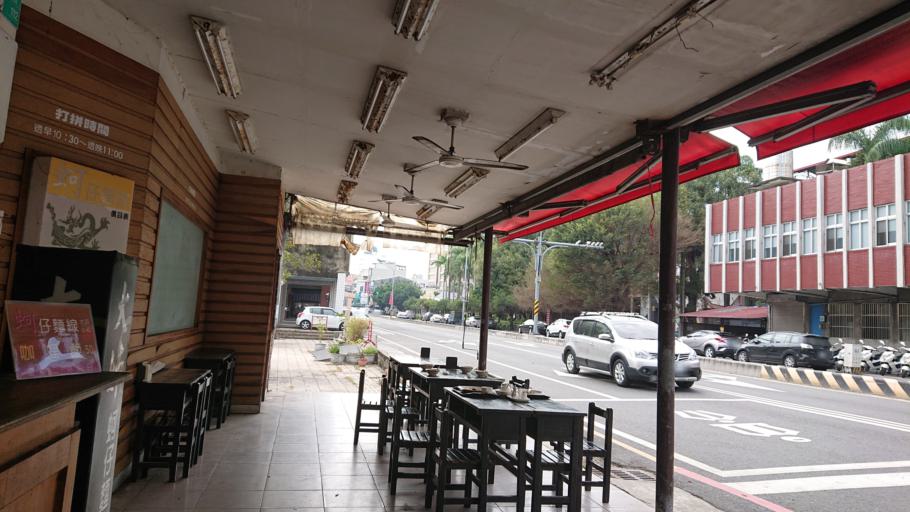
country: TW
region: Taiwan
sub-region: Tainan
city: Tainan
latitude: 23.0017
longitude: 120.2029
